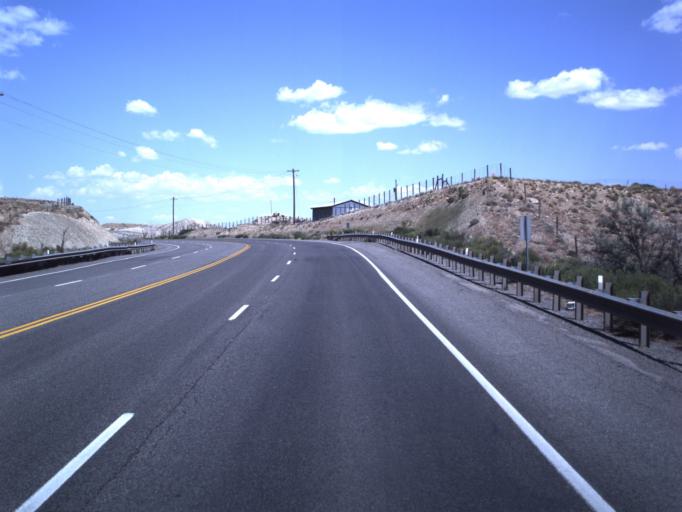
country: US
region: Utah
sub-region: Emery County
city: Huntington
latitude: 39.3390
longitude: -110.9471
